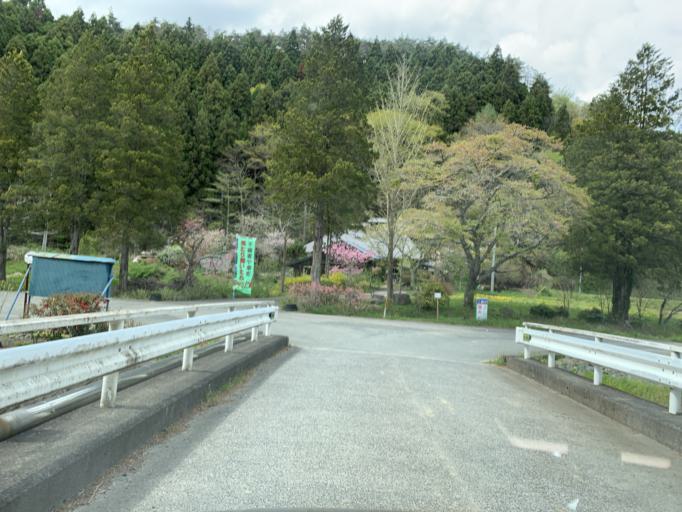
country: JP
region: Iwate
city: Ichinoseki
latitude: 38.7875
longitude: 141.4235
